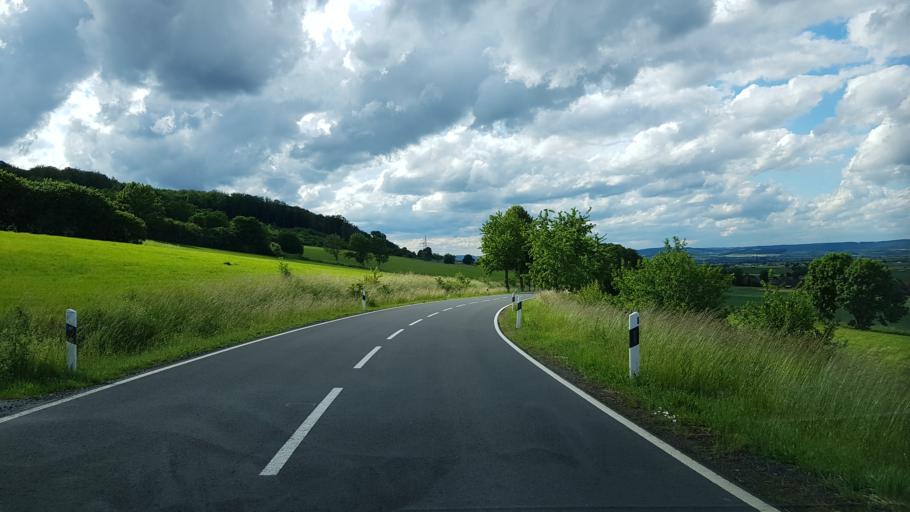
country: DE
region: Lower Saxony
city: Moringen
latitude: 51.7338
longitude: 9.8868
